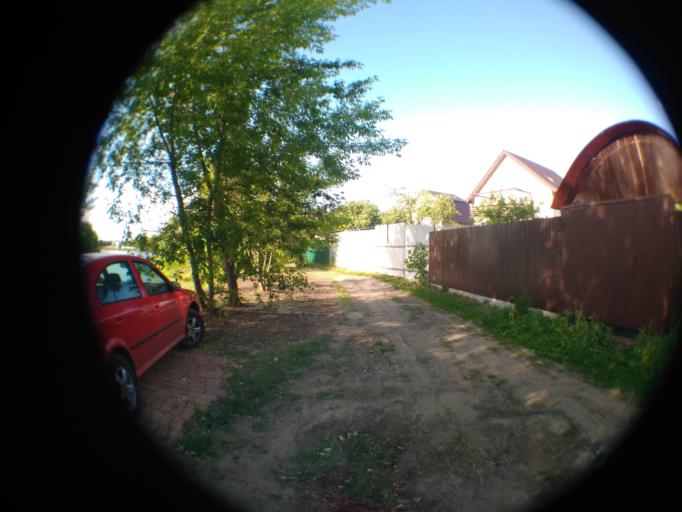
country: RU
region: Moskovskaya
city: Zhukovskiy
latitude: 55.5795
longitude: 38.1029
